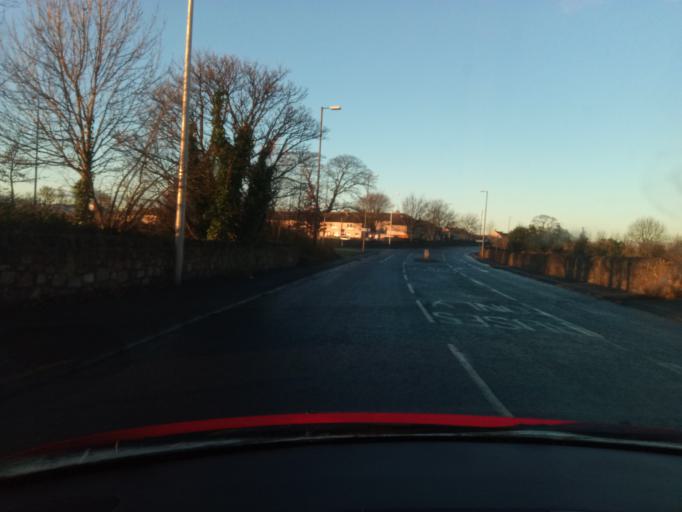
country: GB
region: Scotland
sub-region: East Lothian
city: Prestonpans
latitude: 55.9423
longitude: -3.0130
